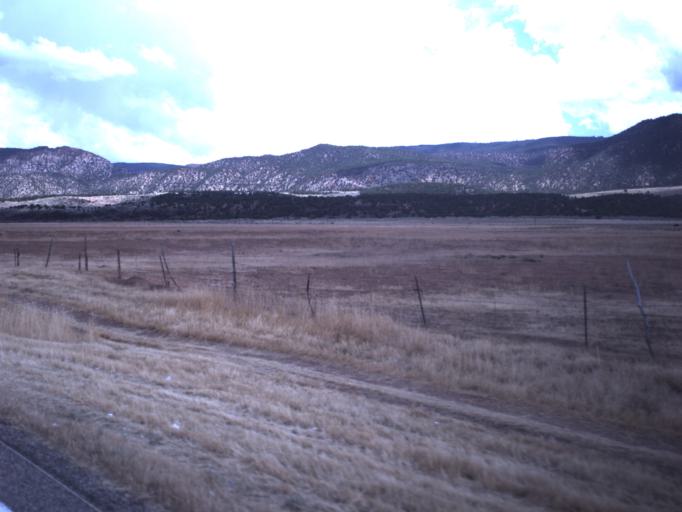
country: US
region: Utah
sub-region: Iron County
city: Parowan
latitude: 37.8707
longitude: -112.7944
